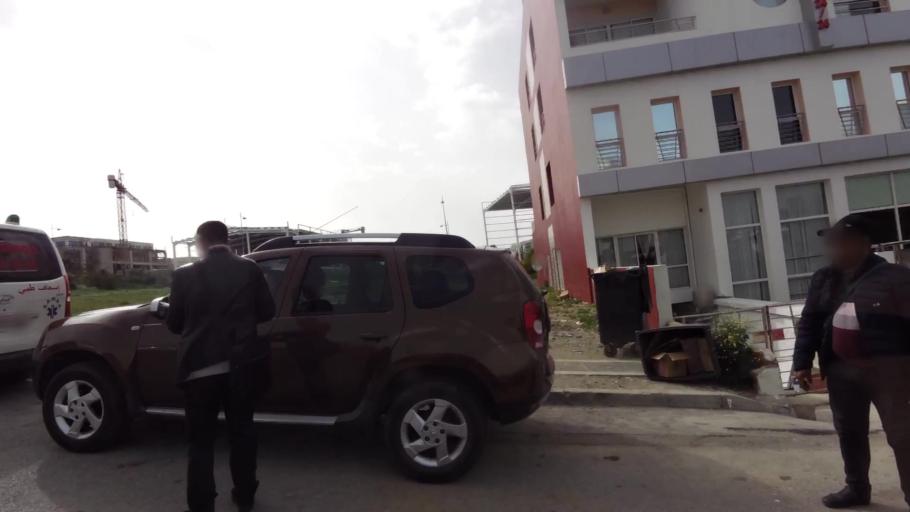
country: MA
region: Tanger-Tetouan
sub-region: Tanger-Assilah
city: Boukhalef
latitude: 35.7142
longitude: -5.9060
